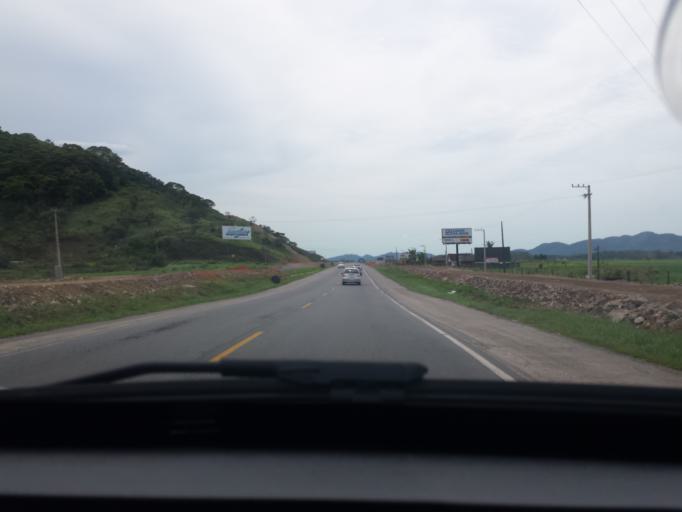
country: BR
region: Santa Catarina
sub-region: Gaspar
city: Gaspar
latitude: -26.8935
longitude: -48.9081
